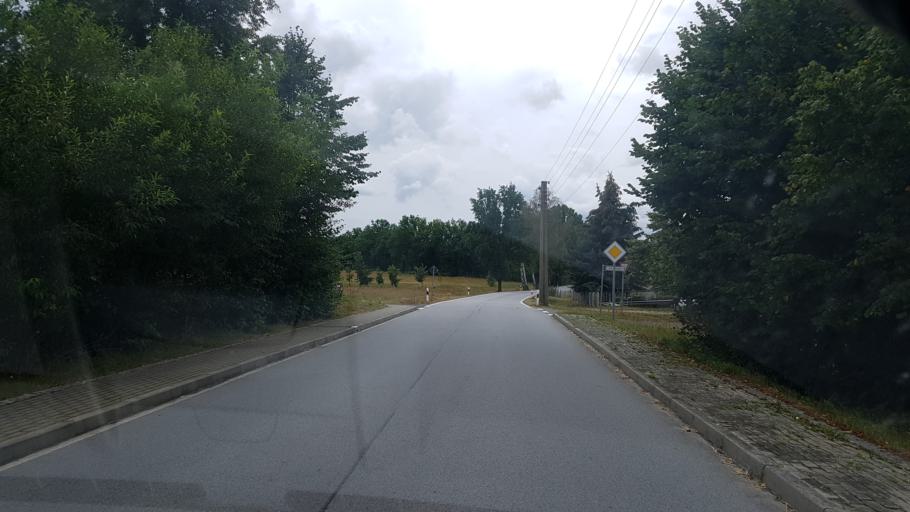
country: DE
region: Saxony
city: Rietschen
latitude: 51.3806
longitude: 14.7335
